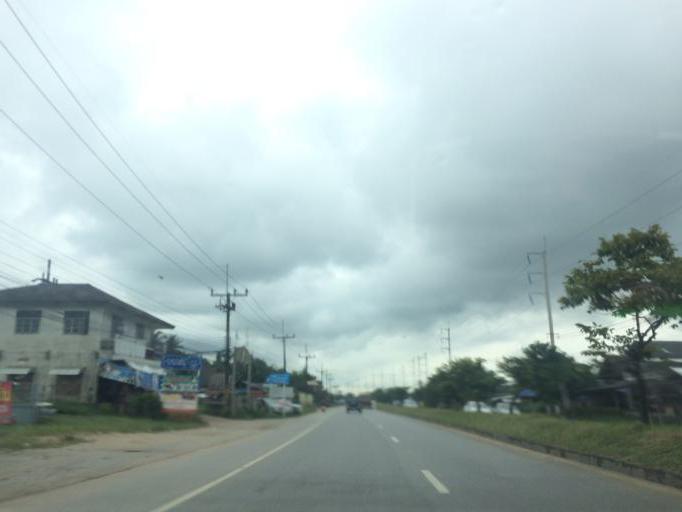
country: TH
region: Chiang Rai
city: Mae Chan
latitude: 20.0717
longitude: 99.8755
